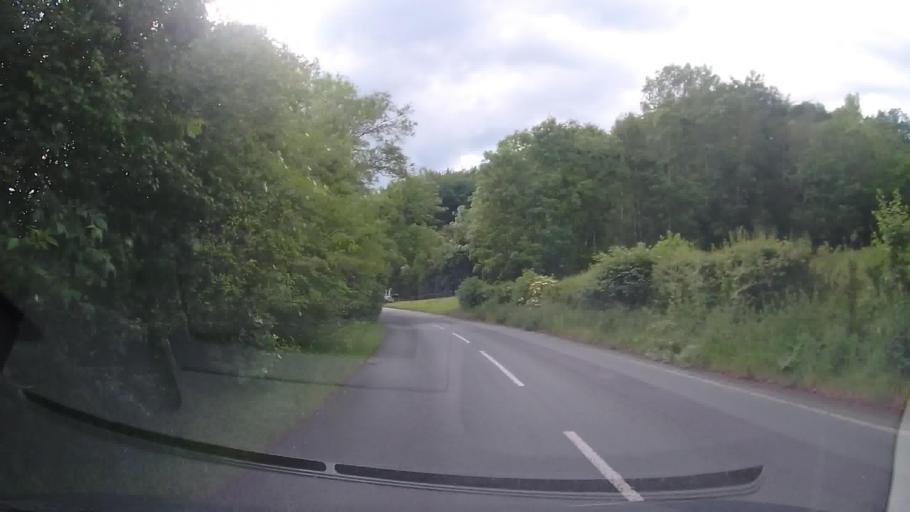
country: GB
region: England
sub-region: Telford and Wrekin
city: Ironbridge
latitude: 52.6381
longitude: -2.5144
